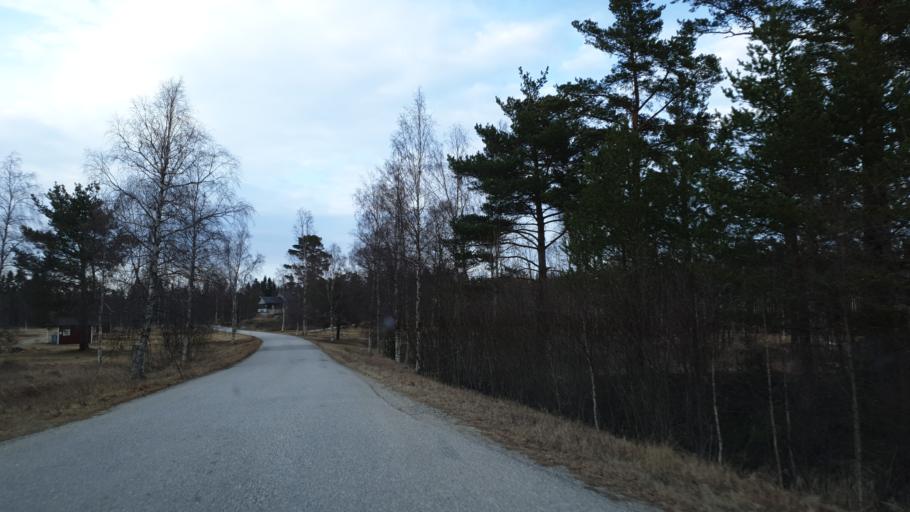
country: SE
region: Vaesternorrland
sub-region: Sundsvalls Kommun
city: Njurundabommen
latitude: 62.0189
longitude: 17.4065
